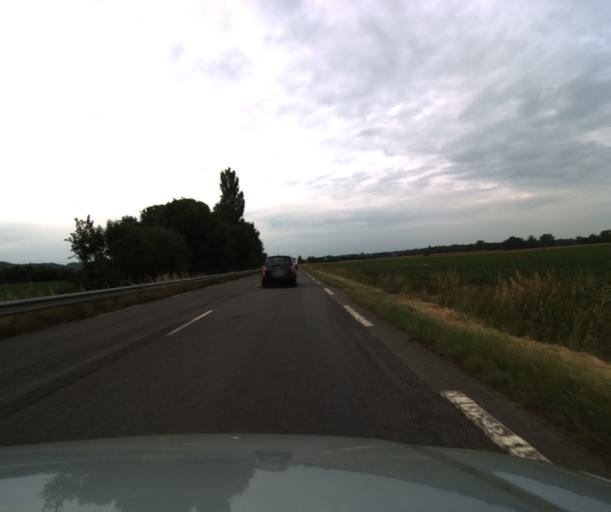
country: FR
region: Midi-Pyrenees
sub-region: Departement des Hautes-Pyrenees
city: Rabastens-de-Bigorre
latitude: 43.3501
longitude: 0.1365
